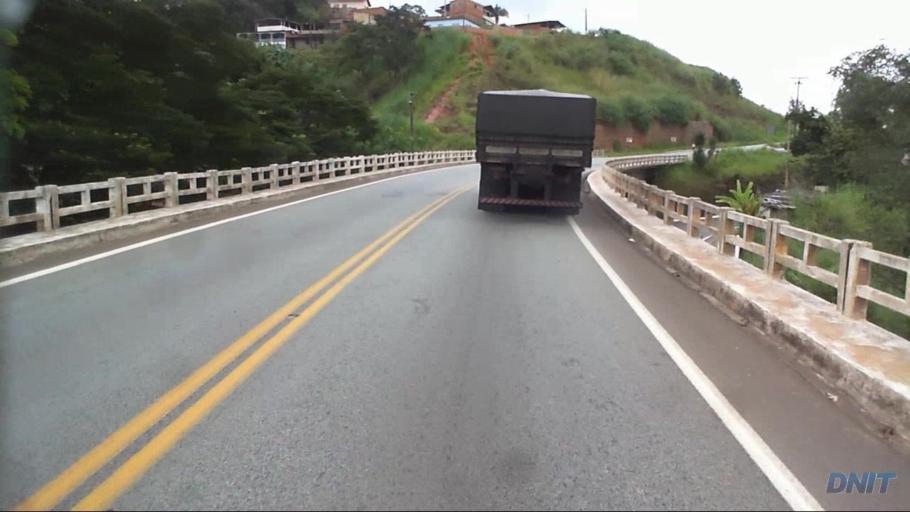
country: BR
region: Minas Gerais
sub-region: Joao Monlevade
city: Joao Monlevade
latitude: -19.8289
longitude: -43.0889
